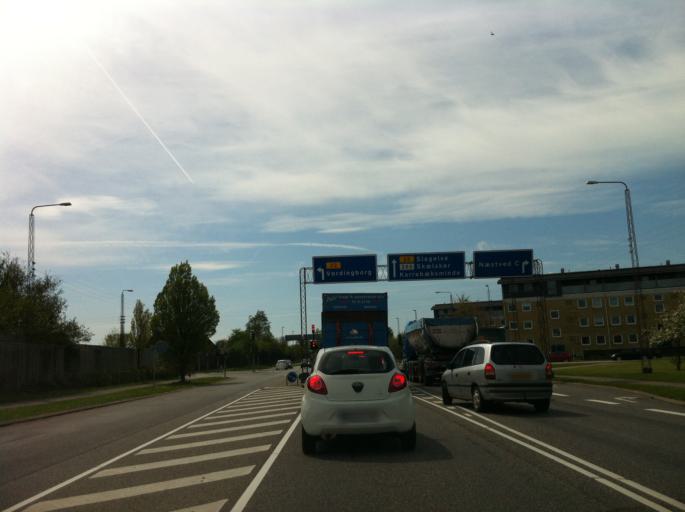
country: DK
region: Zealand
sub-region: Naestved Kommune
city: Naestved
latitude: 55.2124
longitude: 11.7551
